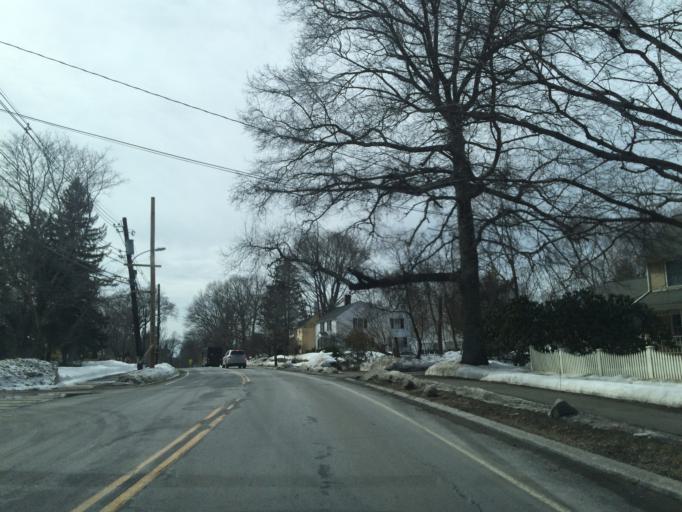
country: US
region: Massachusetts
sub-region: Middlesex County
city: Lexington
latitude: 42.4478
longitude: -71.2444
